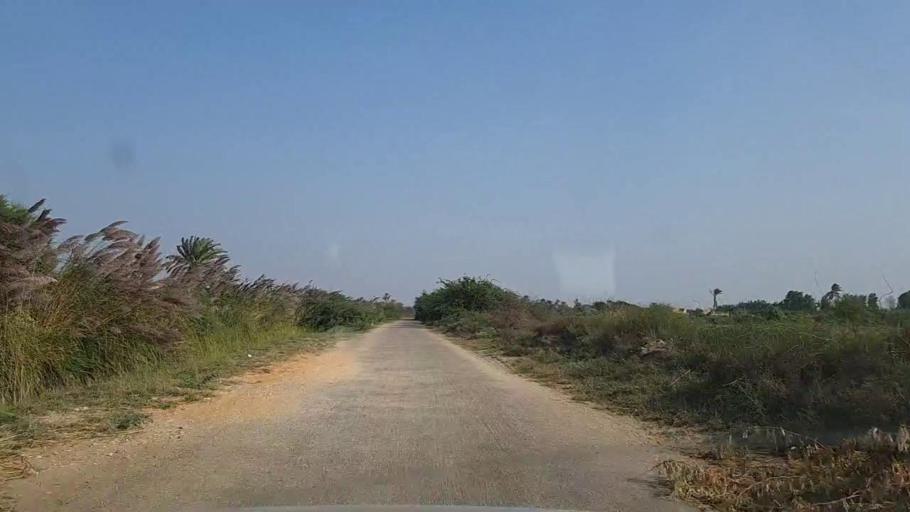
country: PK
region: Sindh
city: Mirpur Sakro
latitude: 24.5947
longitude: 67.6036
